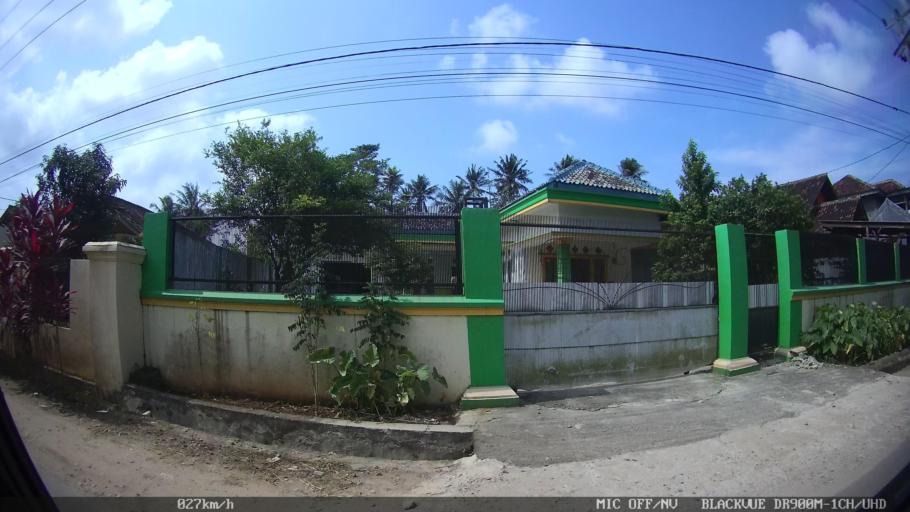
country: ID
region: Lampung
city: Kedaton
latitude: -5.3421
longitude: 105.2870
